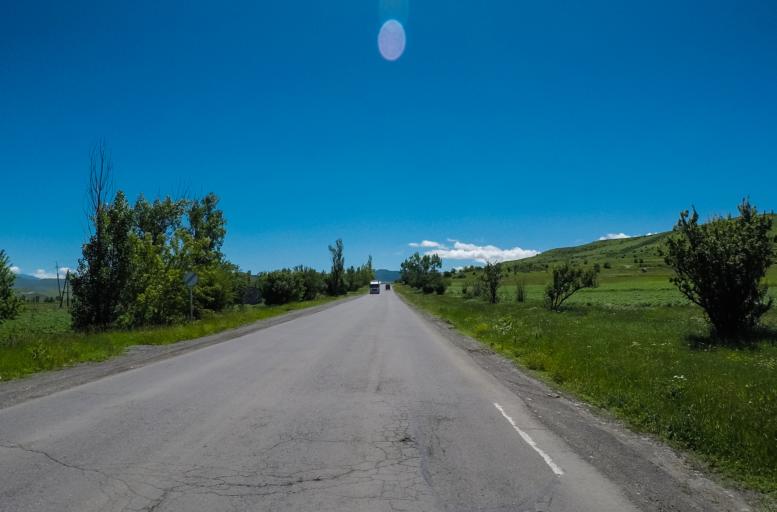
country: GE
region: Samtskhe-Javakheti
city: Akhaltsikhe
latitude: 41.6417
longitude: 43.0270
